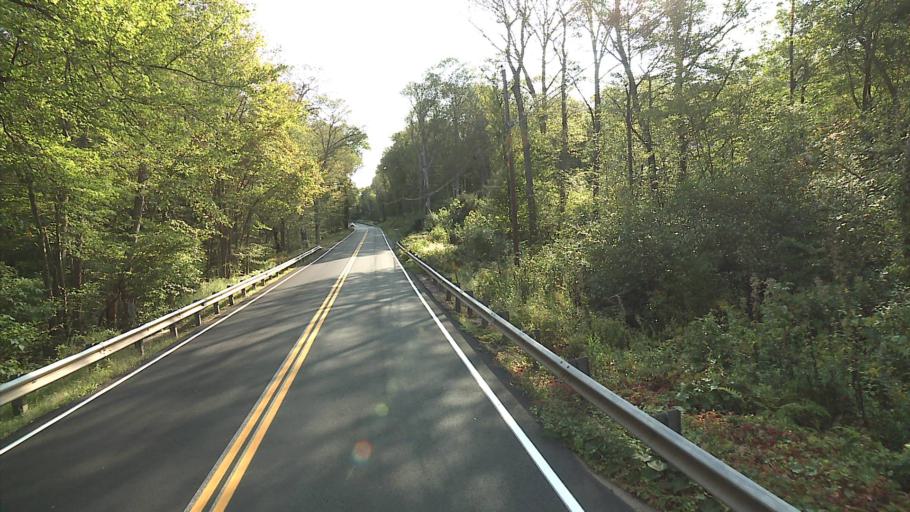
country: US
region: Connecticut
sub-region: Tolland County
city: Hebron
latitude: 41.7243
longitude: -72.3989
